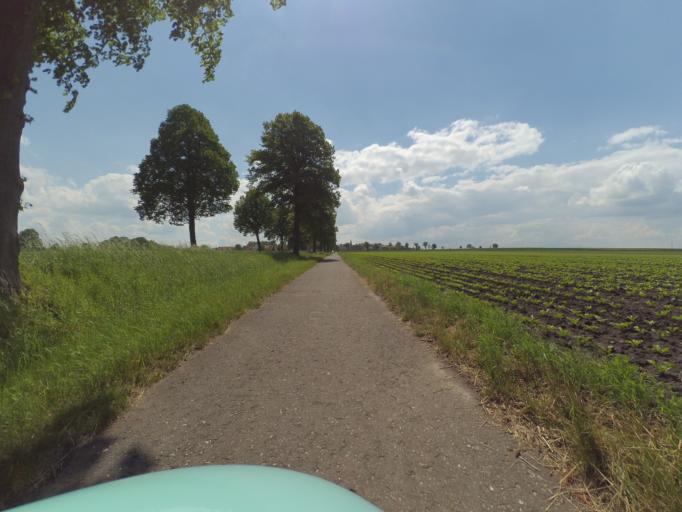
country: DE
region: Lower Saxony
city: Hohenhameln
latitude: 52.2274
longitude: 10.0341
